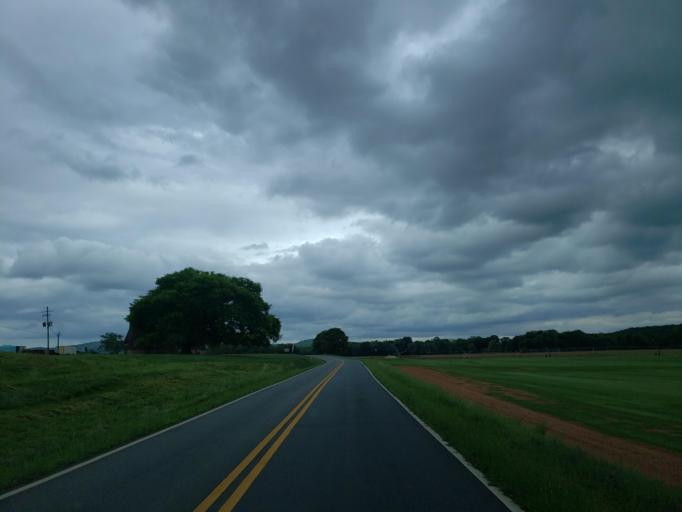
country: US
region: Georgia
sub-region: Bartow County
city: Cartersville
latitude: 34.1260
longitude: -84.8187
